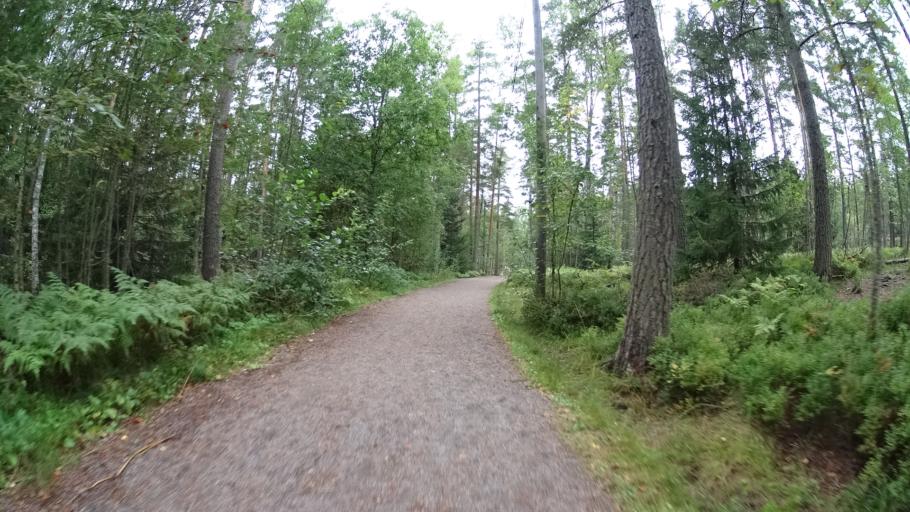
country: FI
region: Uusimaa
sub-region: Helsinki
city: Kauniainen
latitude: 60.1785
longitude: 24.7251
